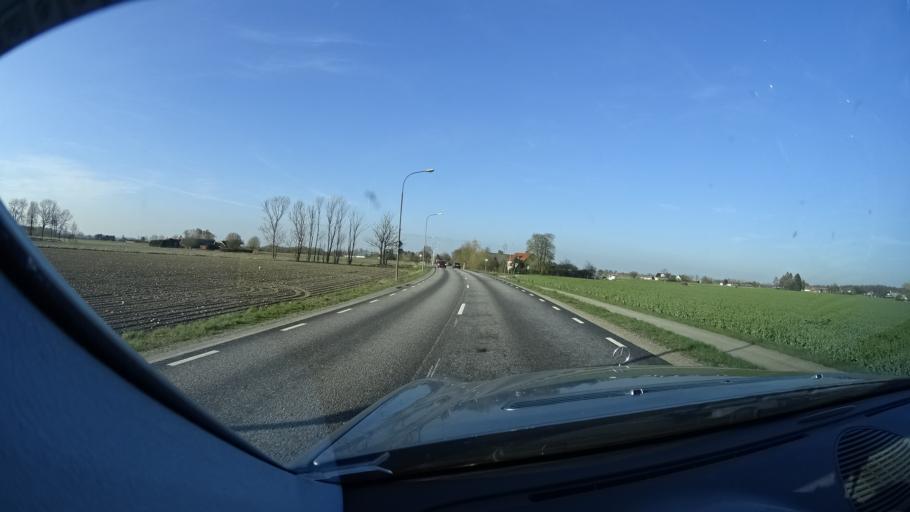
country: SE
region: Skane
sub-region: Eslovs Kommun
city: Eslov
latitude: 55.8458
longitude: 13.3410
